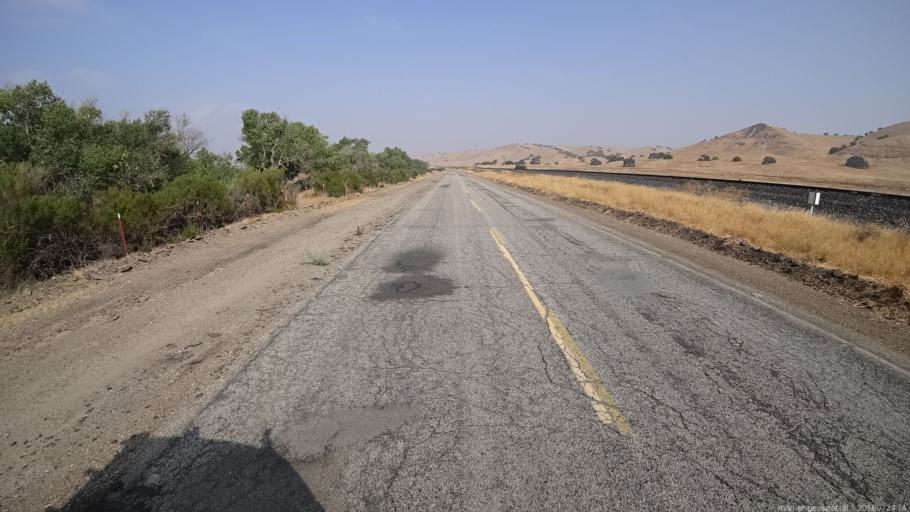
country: US
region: California
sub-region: San Luis Obispo County
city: San Miguel
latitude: 35.8554
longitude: -120.7610
